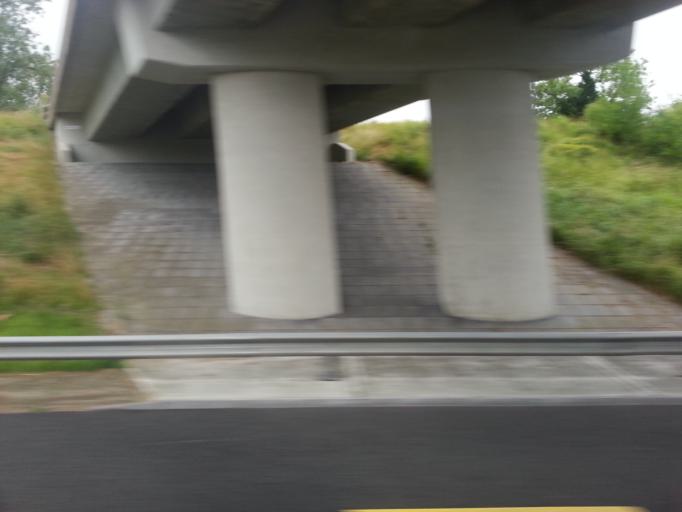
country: IE
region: Leinster
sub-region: Kilkenny
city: Kilkenny
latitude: 52.6442
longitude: -7.1824
